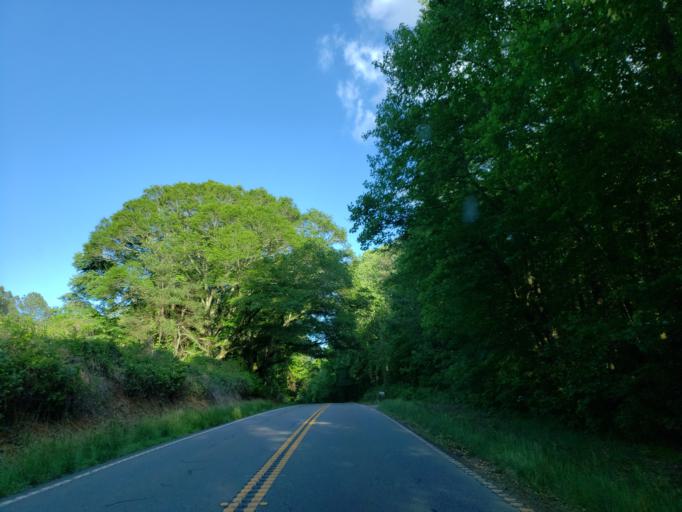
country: US
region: Georgia
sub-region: Bartow County
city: Rydal
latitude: 34.3484
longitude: -84.5898
